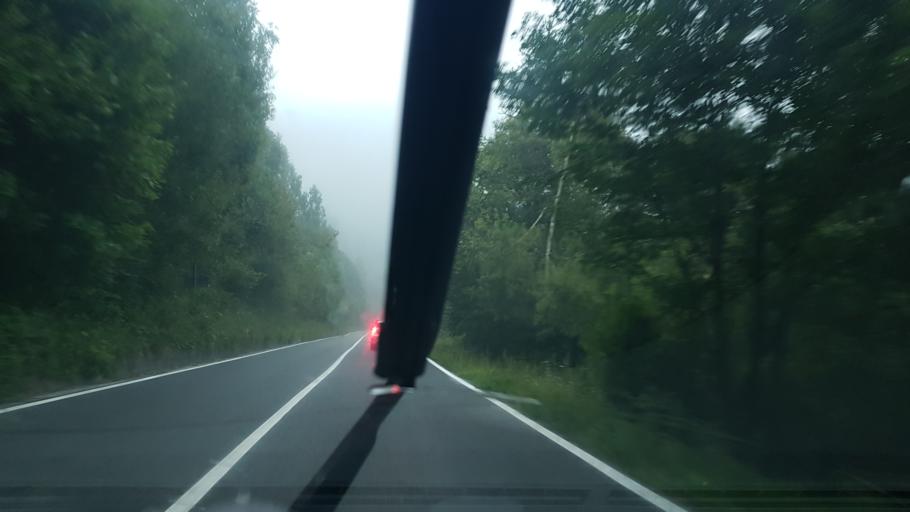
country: IT
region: Piedmont
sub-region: Provincia di Cuneo
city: Frabosa Soprana
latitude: 44.2606
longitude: 7.7669
